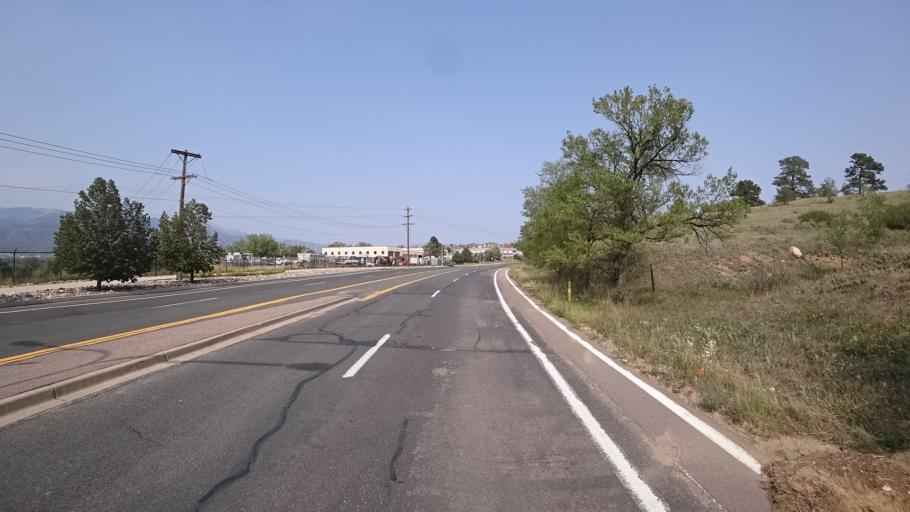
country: US
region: Colorado
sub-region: El Paso County
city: Colorado Springs
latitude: 38.8135
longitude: -104.8030
